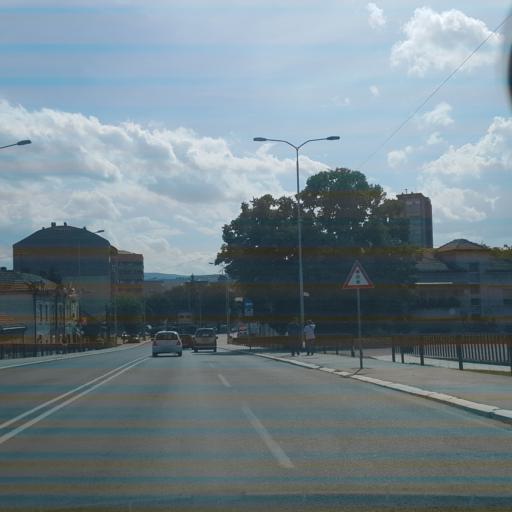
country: RS
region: Central Serbia
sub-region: Nisavski Okrug
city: Nis
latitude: 43.3261
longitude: 21.9029
